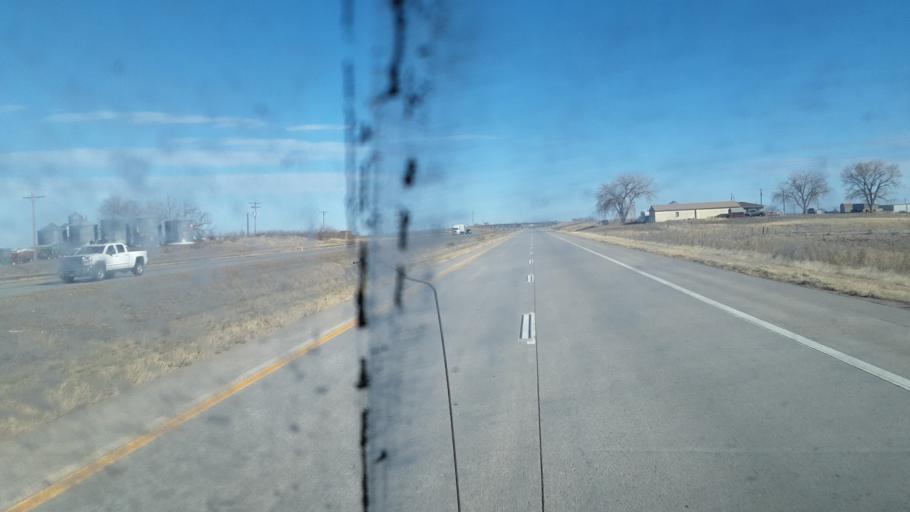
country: US
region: Colorado
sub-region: Morgan County
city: Fort Morgan
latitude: 40.2322
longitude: -104.1046
